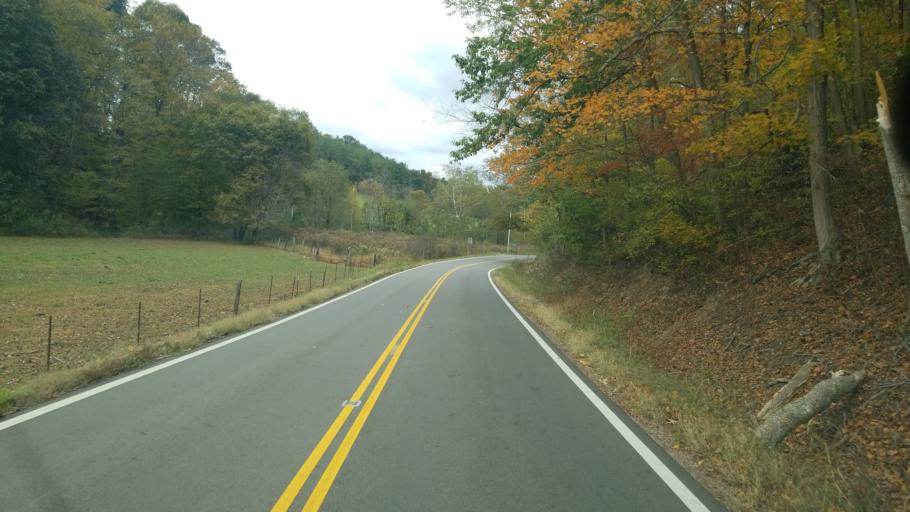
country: US
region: Ohio
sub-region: Jackson County
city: Wellston
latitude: 39.1643
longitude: -82.6266
